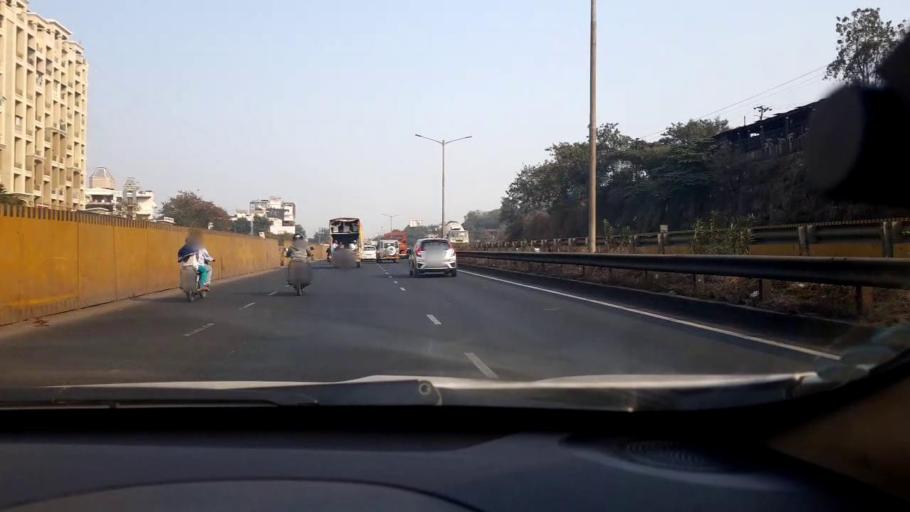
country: IN
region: Maharashtra
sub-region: Pune Division
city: Kharakvasla
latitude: 18.5084
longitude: 73.7785
